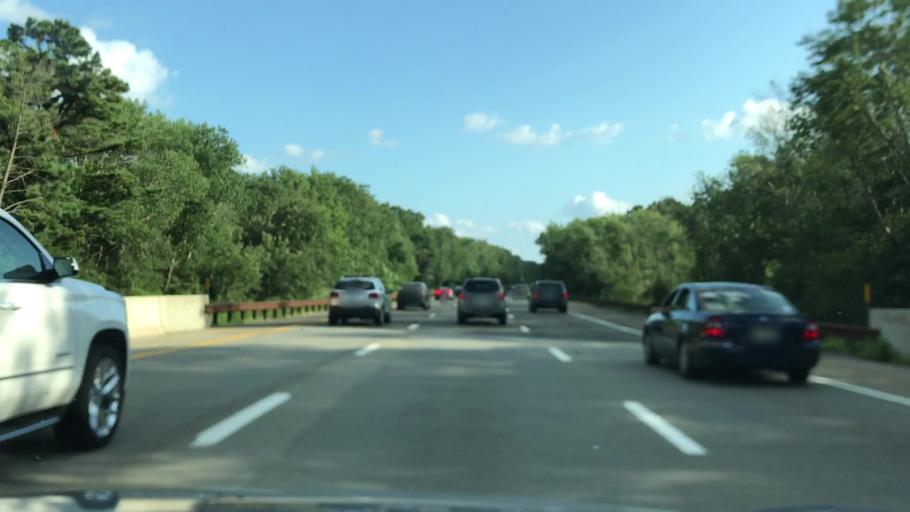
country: US
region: New Jersey
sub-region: Ocean County
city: Forked River
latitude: 39.8849
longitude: -74.2127
